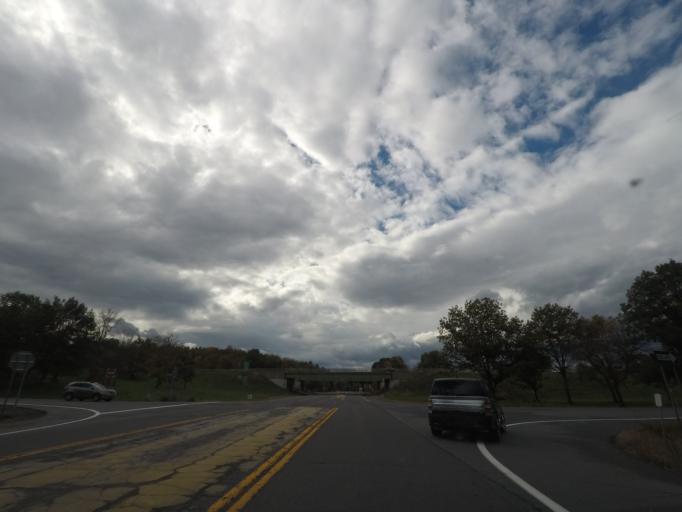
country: US
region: New York
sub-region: Rensselaer County
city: East Greenbush
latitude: 42.5799
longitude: -73.6775
